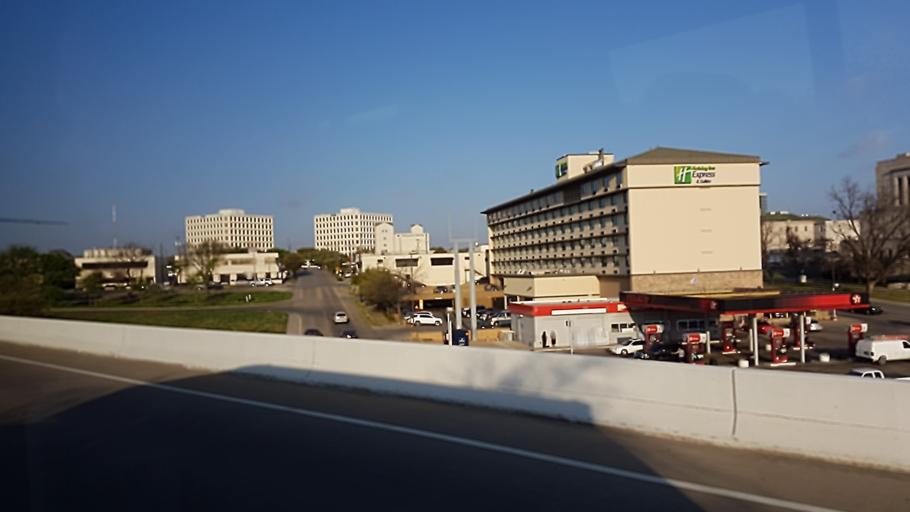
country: US
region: Texas
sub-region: Tarrant County
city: Fort Worth
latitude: 32.7461
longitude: -97.3370
